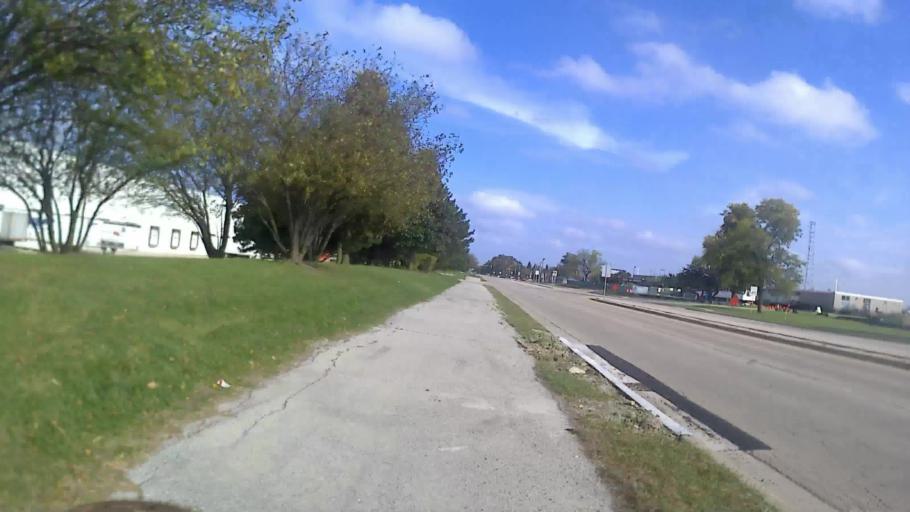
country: US
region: Illinois
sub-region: DuPage County
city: Warrenville
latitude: 41.8078
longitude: -88.1928
